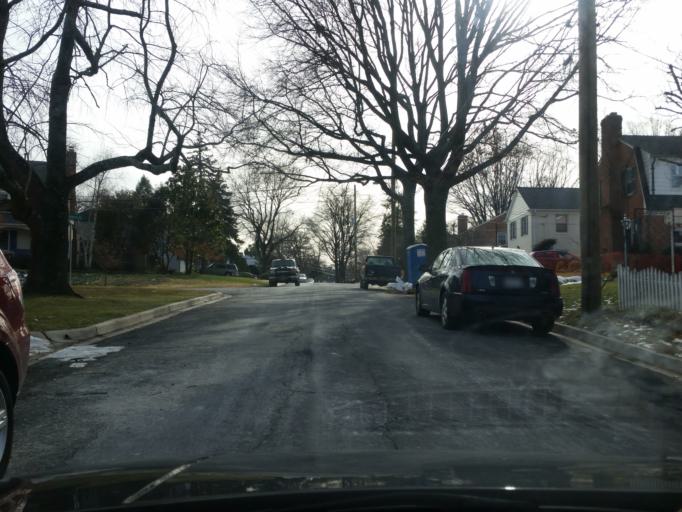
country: US
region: Maryland
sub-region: Montgomery County
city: Chevy Chase
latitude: 38.9829
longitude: -77.0627
